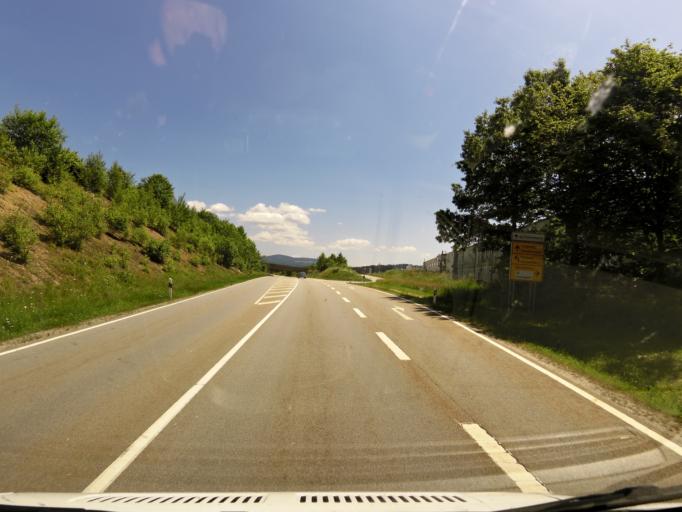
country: DE
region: Bavaria
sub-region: Lower Bavaria
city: Hutthurm
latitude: 48.6782
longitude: 13.4830
